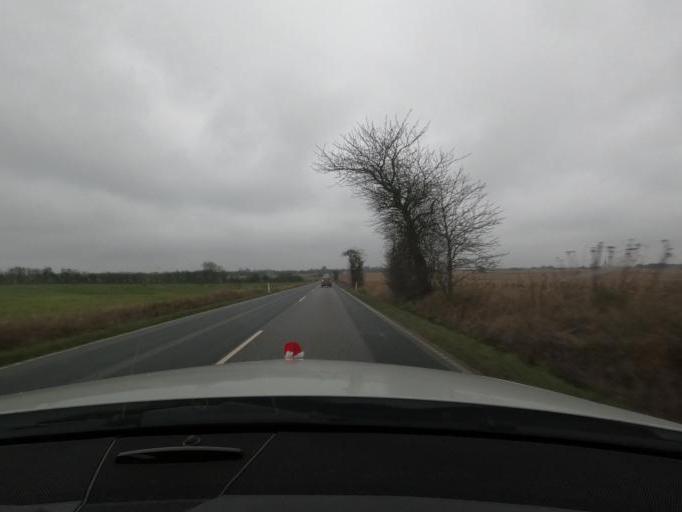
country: DK
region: South Denmark
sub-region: Haderslev Kommune
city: Starup
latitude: 55.1990
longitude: 9.5357
